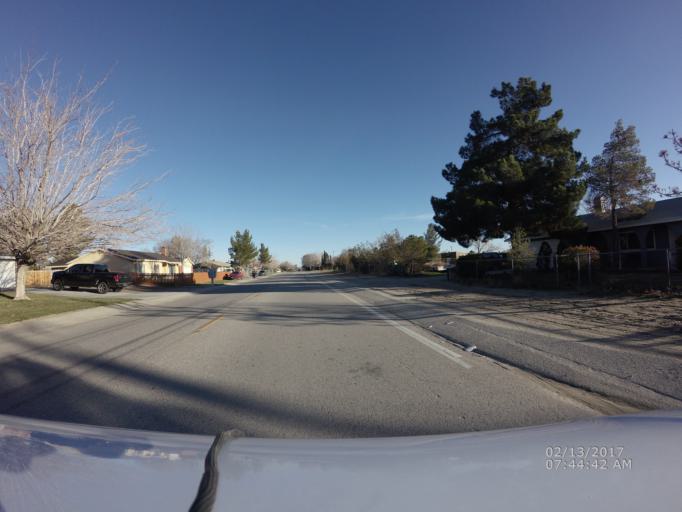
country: US
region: California
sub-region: Los Angeles County
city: Littlerock
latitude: 34.5523
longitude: -117.9582
